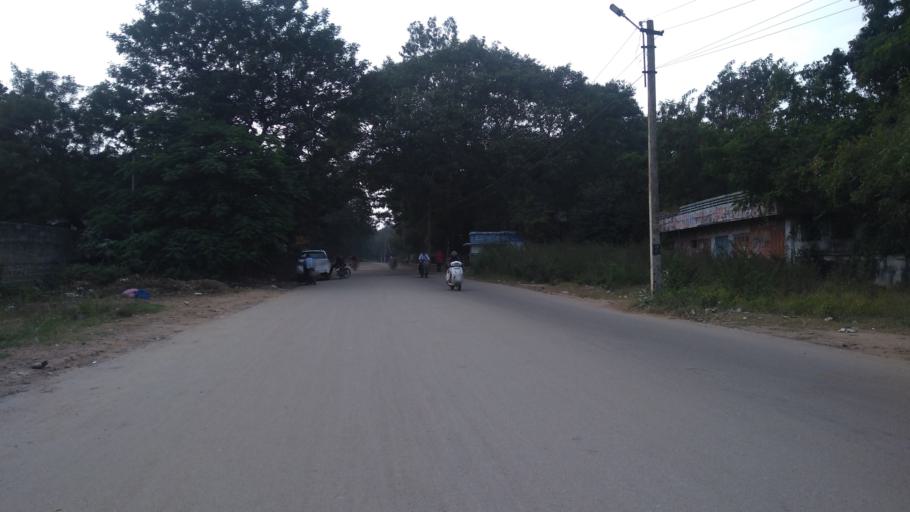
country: IN
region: Telangana
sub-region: Medak
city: Serilingampalle
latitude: 17.5005
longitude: 78.3121
